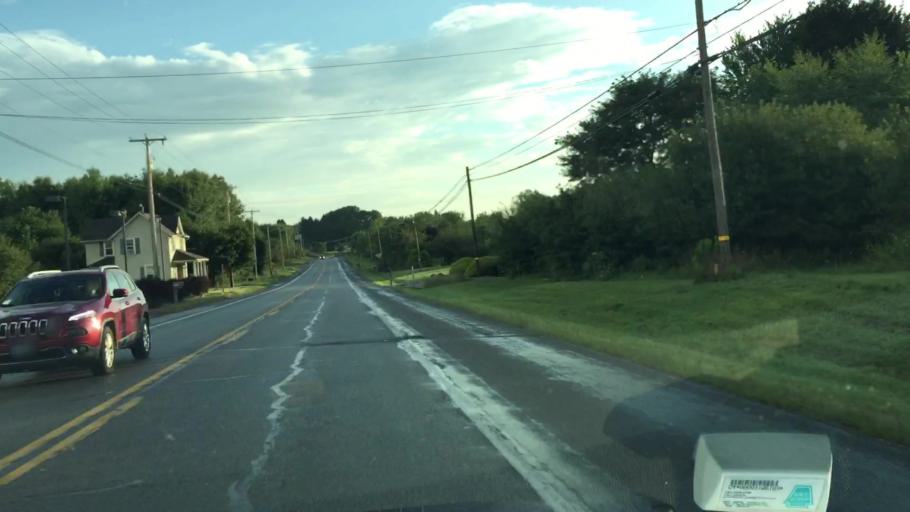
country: US
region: Pennsylvania
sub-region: Butler County
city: Meridian
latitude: 40.8396
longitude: -79.9977
